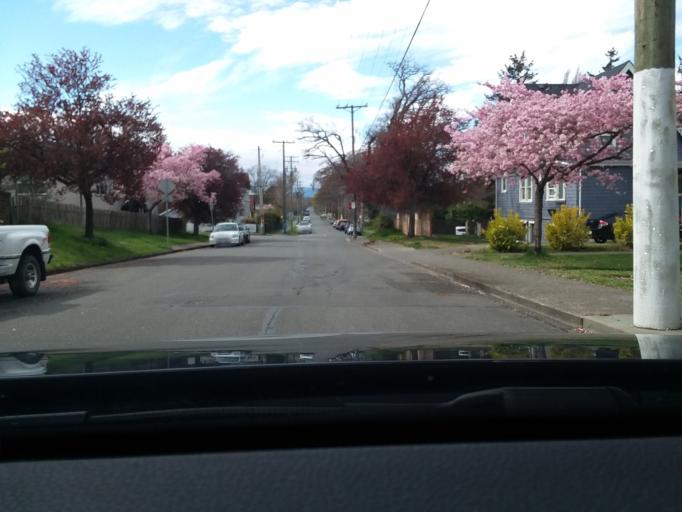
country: CA
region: British Columbia
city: Victoria
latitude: 48.4317
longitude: -123.3489
